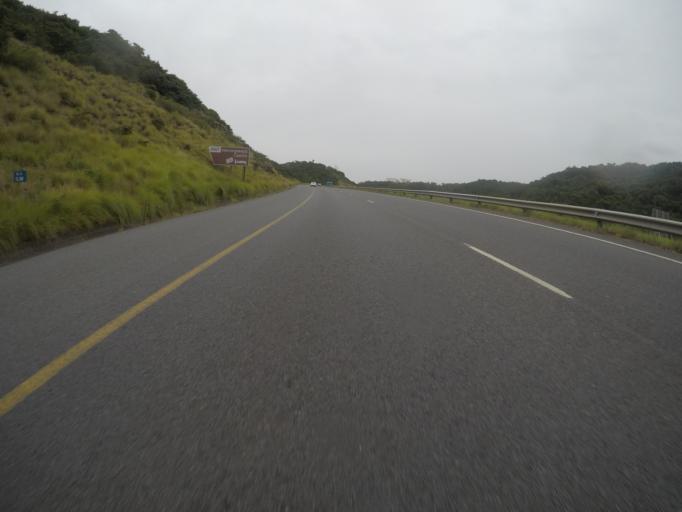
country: ZA
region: Eastern Cape
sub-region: Buffalo City Metropolitan Municipality
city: East London
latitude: -32.9693
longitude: 27.9124
